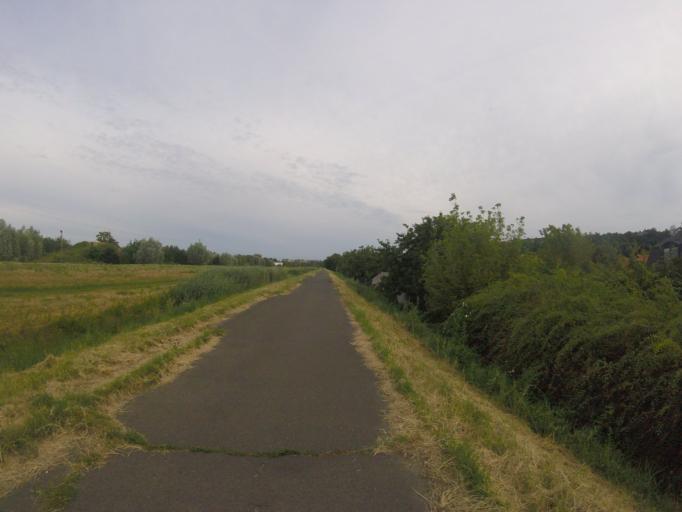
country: HU
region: Pest
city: Budakalasz
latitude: 47.6154
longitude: 19.0574
